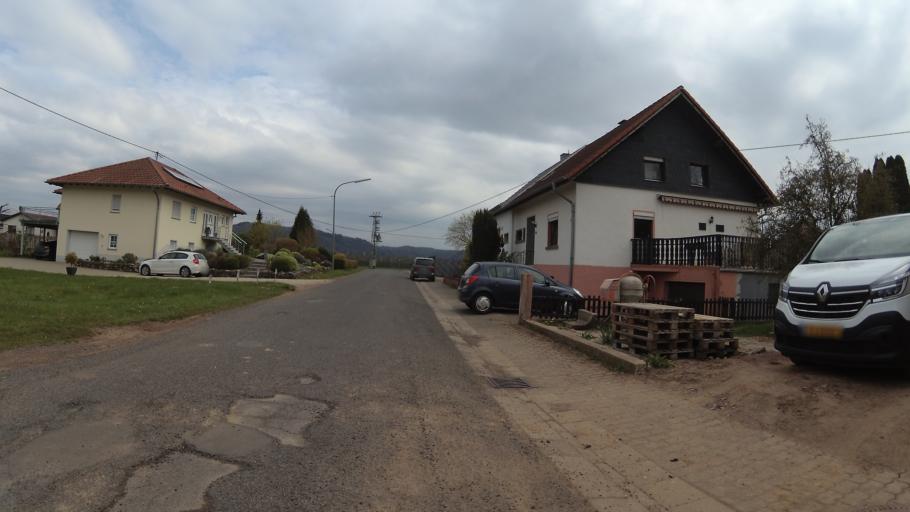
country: DE
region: Saarland
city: Merzig
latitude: 49.4519
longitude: 6.6062
